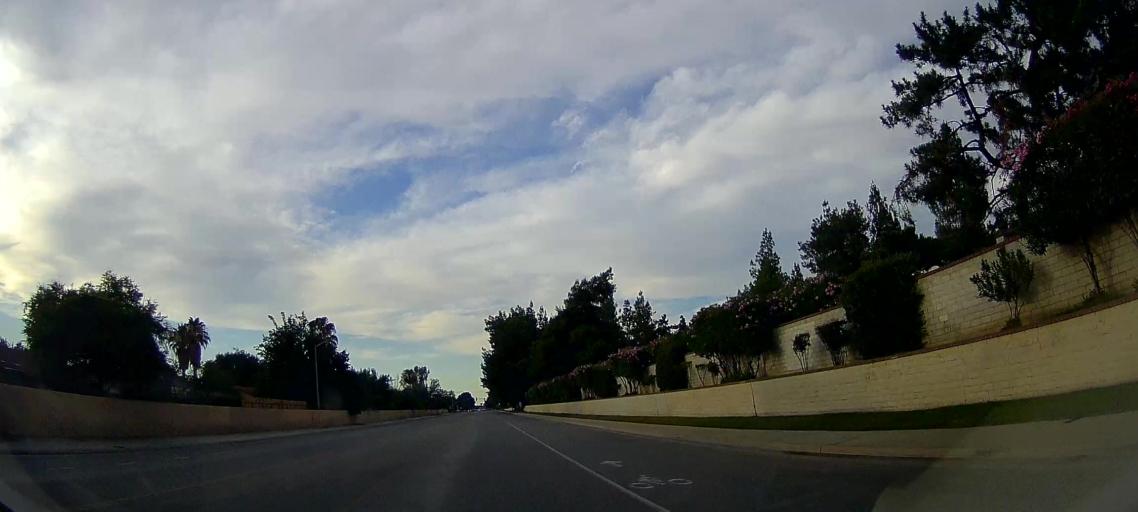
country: US
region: California
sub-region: Kern County
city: Bakersfield
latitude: 35.3220
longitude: -119.0478
